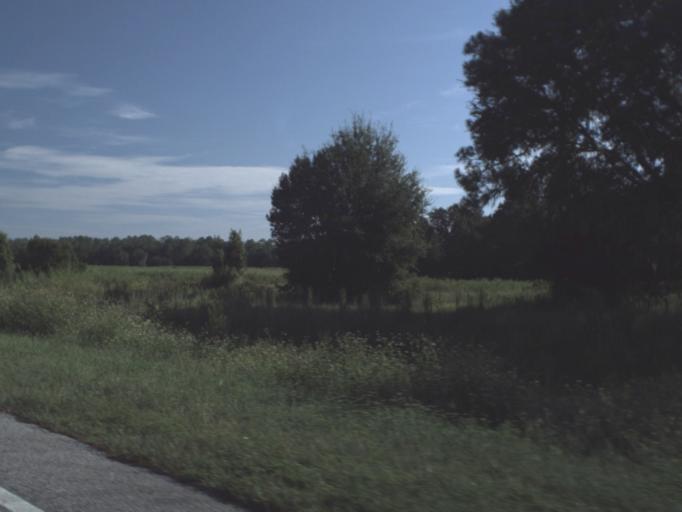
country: US
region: Florida
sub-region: Pasco County
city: Zephyrhills North
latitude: 28.2519
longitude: -82.0555
